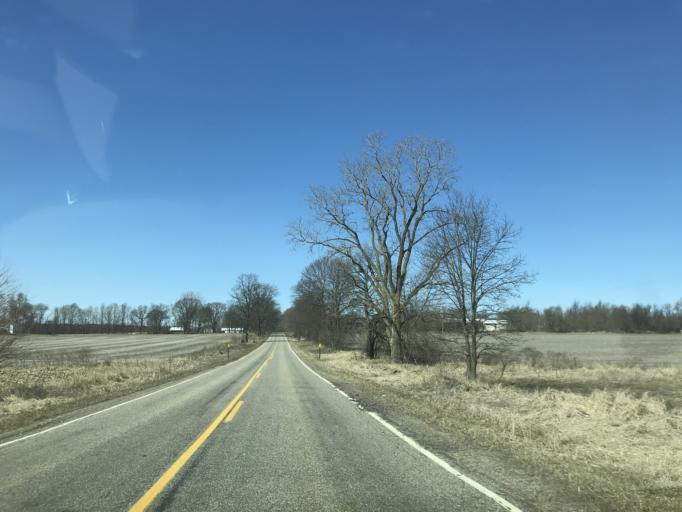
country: US
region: Michigan
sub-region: Hillsdale County
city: Litchfield
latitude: 41.9855
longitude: -84.7335
